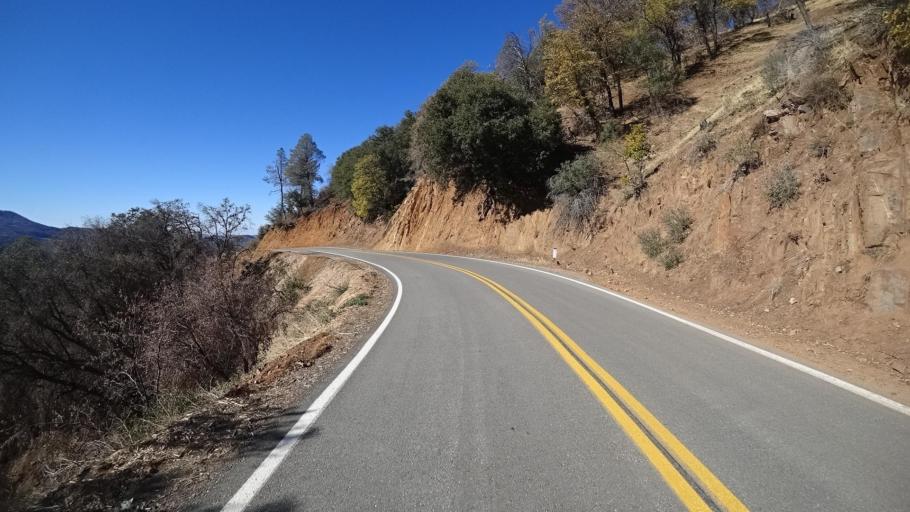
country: US
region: California
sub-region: Kern County
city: Alta Sierra
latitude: 35.7427
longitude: -118.5739
